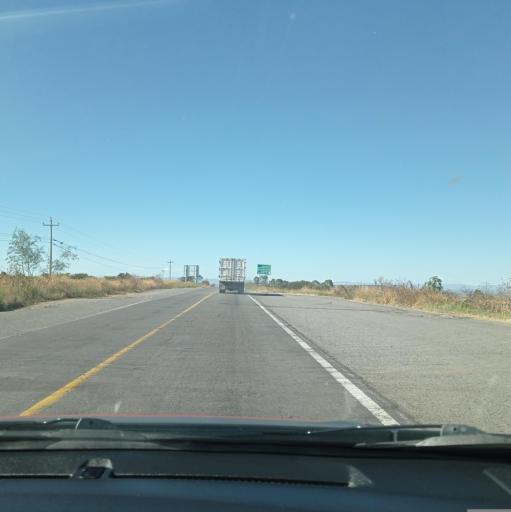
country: MX
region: Jalisco
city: Valle de Guadalupe
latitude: 21.0288
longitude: -102.5510
